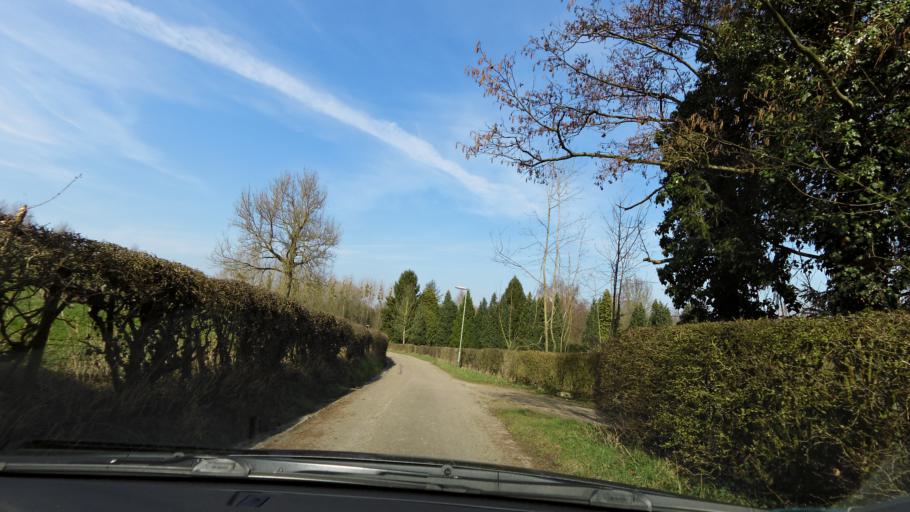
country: NL
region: Limburg
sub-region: Valkenburg aan de Geul
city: Schin op Geul
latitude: 50.8274
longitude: 5.8872
